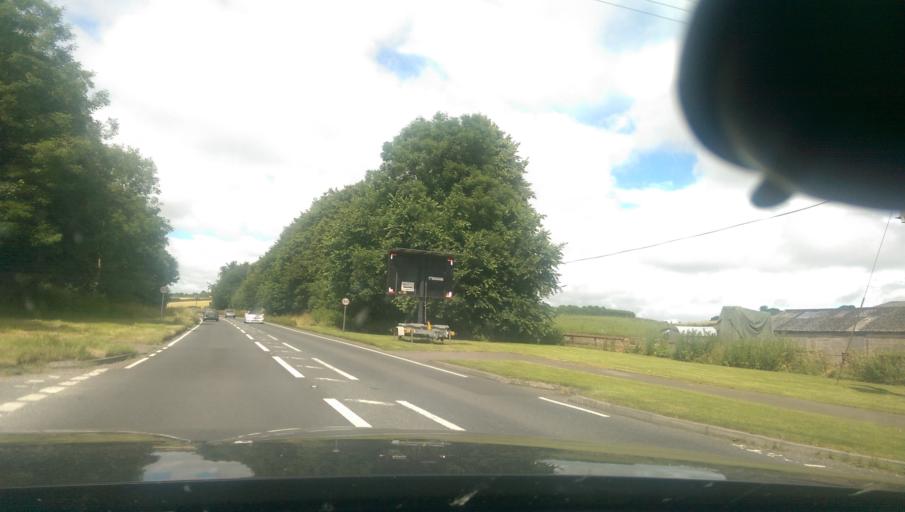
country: GB
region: England
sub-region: Wiltshire
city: Chicklade
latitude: 51.1097
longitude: -2.1301
